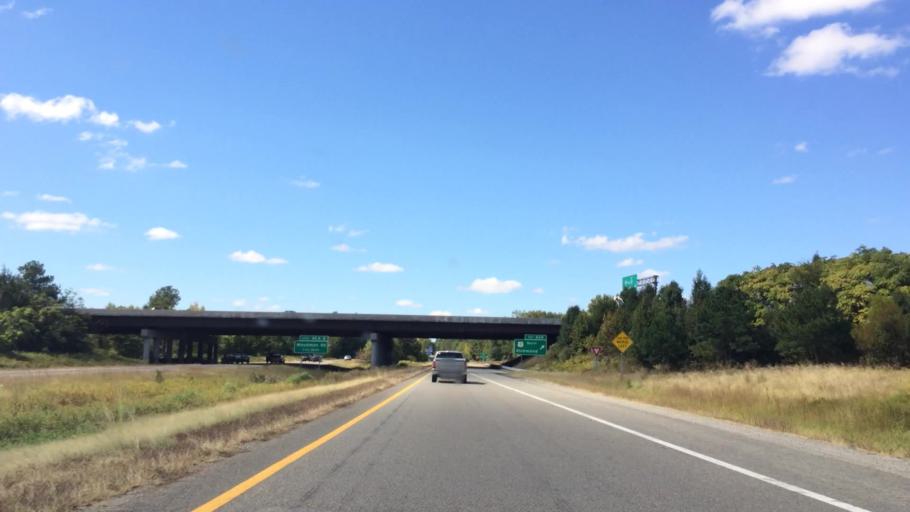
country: US
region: Virginia
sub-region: Henrico County
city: Chamberlayne
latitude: 37.6592
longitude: -77.4583
